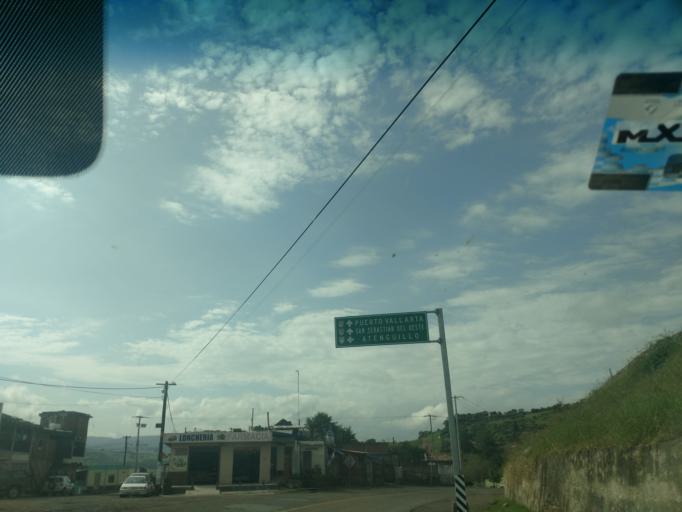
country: MX
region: Jalisco
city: El Salto
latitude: 20.4200
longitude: -104.4993
